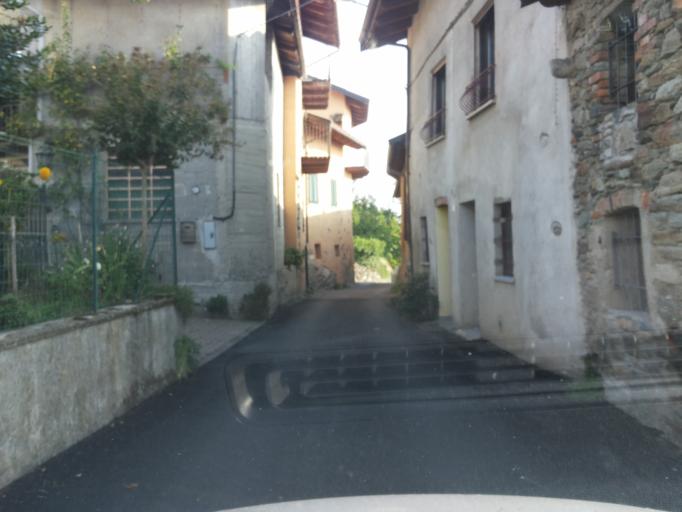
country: IT
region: Piedmont
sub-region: Provincia di Biella
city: Viverone
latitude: 45.4280
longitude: 8.0564
